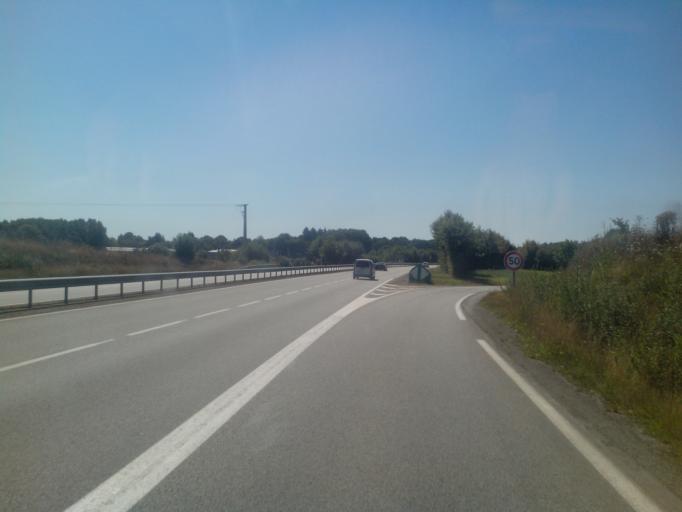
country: FR
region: Brittany
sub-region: Departement des Cotes-d'Armor
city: Loudeac
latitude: 48.1705
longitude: -2.7336
